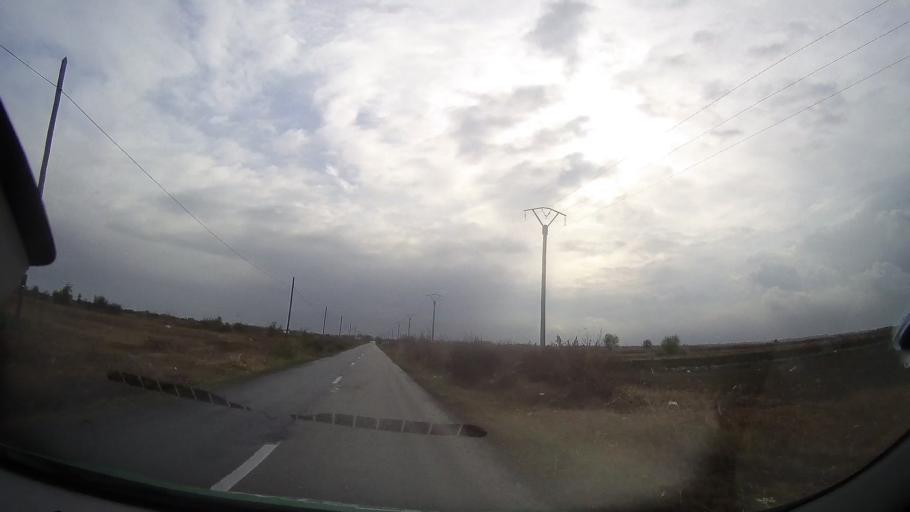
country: RO
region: Ialomita
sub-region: Comuna Fierbinti-Targ
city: Fierbintii de Jos
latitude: 44.7102
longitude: 26.3914
